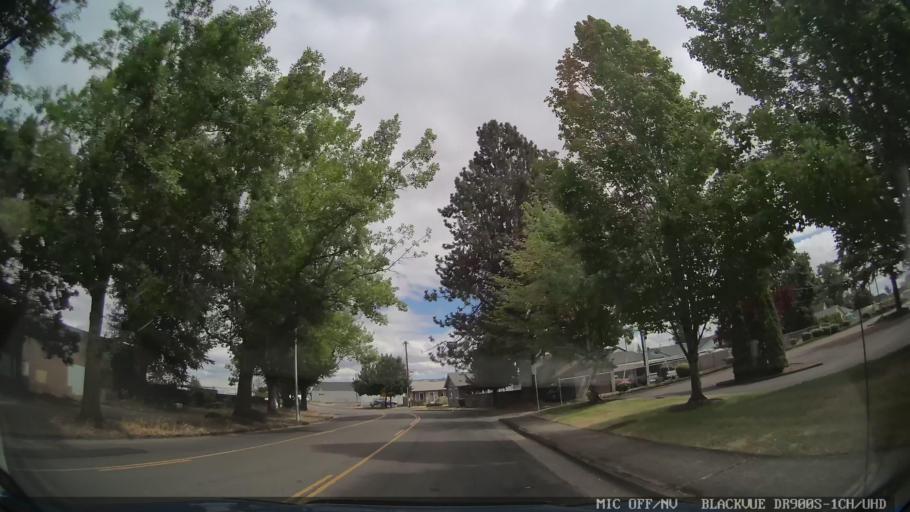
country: US
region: Oregon
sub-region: Marion County
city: Salem
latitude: 44.9566
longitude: -123.0180
